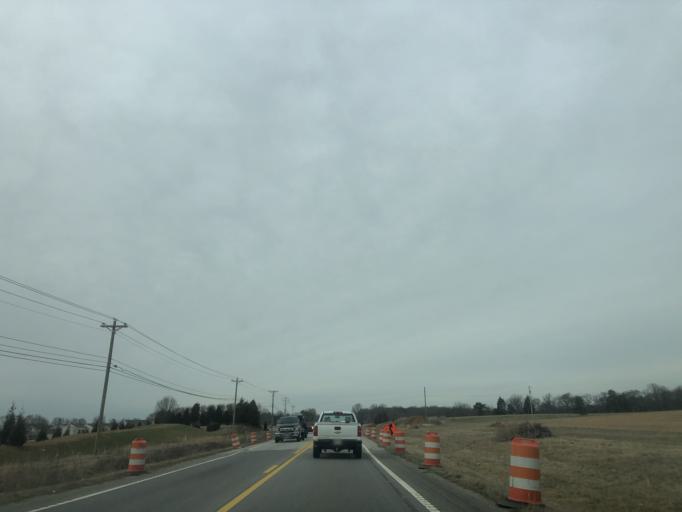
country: US
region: Tennessee
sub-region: Wilson County
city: Mount Juliet
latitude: 36.2504
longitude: -86.4355
